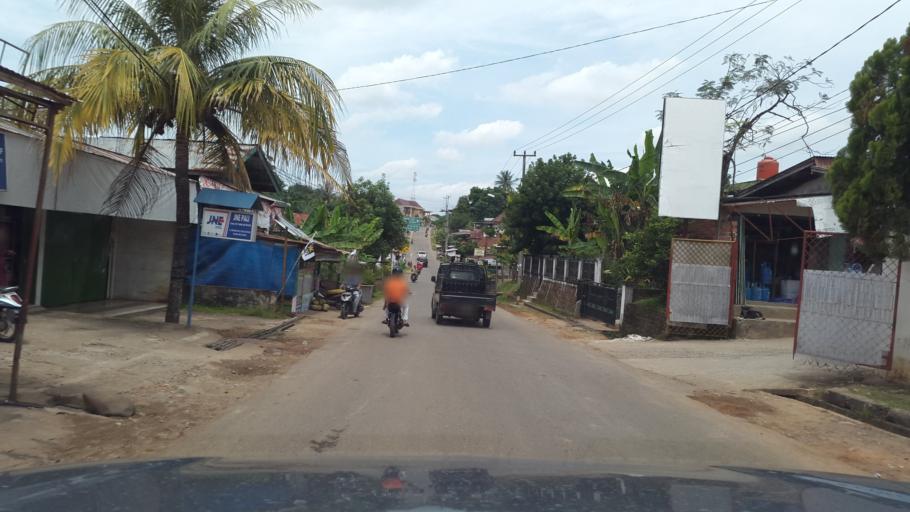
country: ID
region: South Sumatra
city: Gunungmegang Dalam
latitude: -3.2816
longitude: 103.8320
